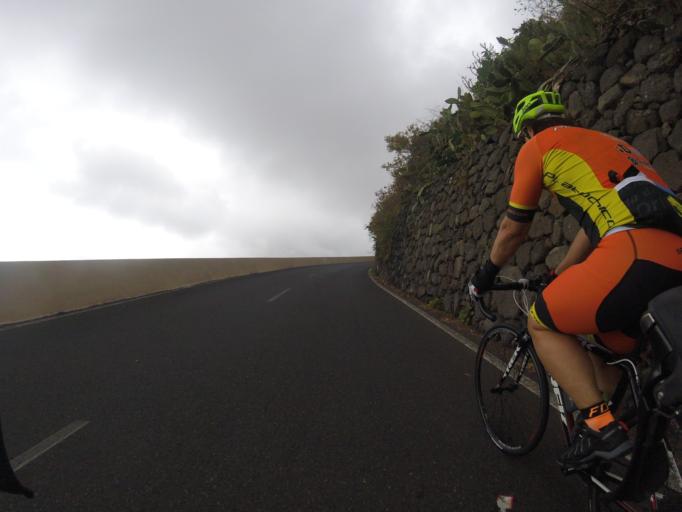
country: ES
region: Canary Islands
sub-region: Provincia de Santa Cruz de Tenerife
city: Guimar
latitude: 28.2963
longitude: -16.4147
